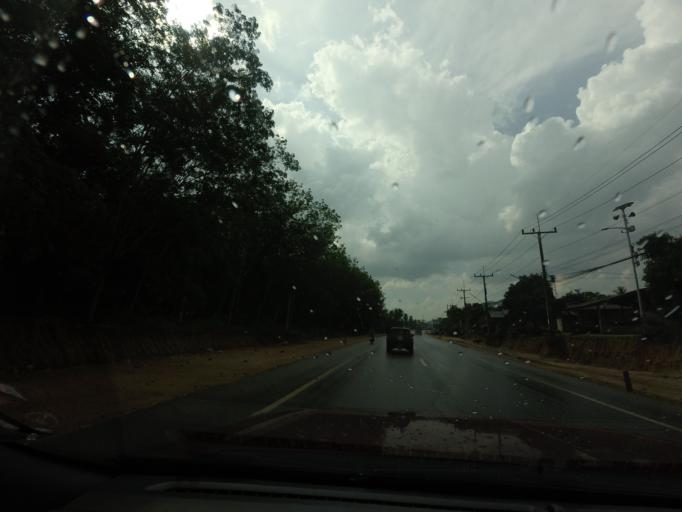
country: TH
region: Yala
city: Krong Pi Nang
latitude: 6.4077
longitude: 101.2803
